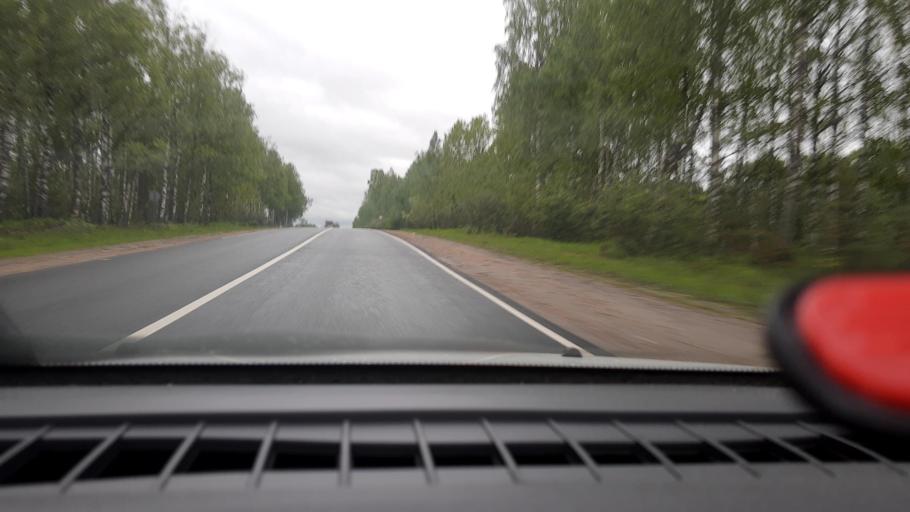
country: RU
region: Nizjnij Novgorod
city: Krasnyye Baki
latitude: 57.0759
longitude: 45.1435
